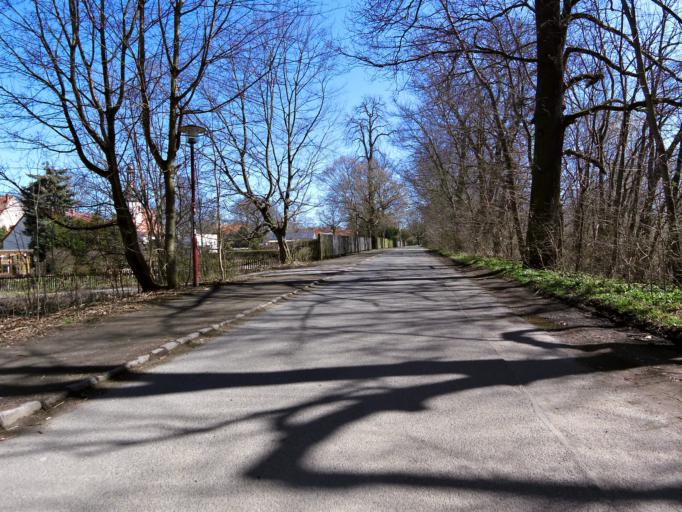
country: DE
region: Saxony
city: Markkleeberg
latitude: 51.2771
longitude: 12.3878
